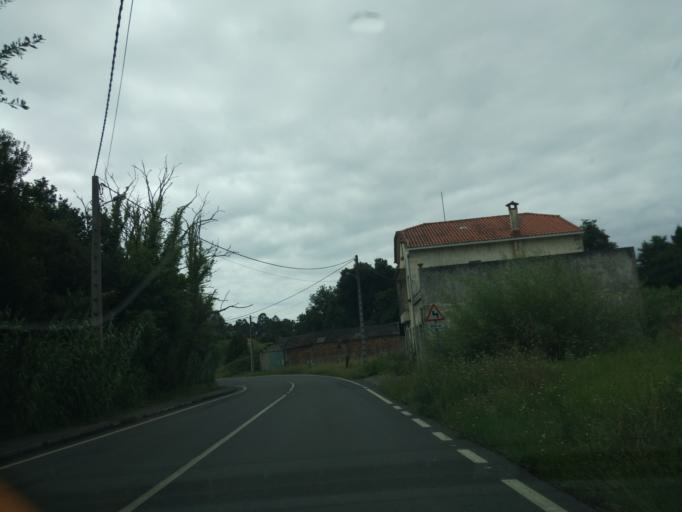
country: ES
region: Galicia
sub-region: Provincia da Coruna
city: Boiro
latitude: 42.6468
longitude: -8.8614
